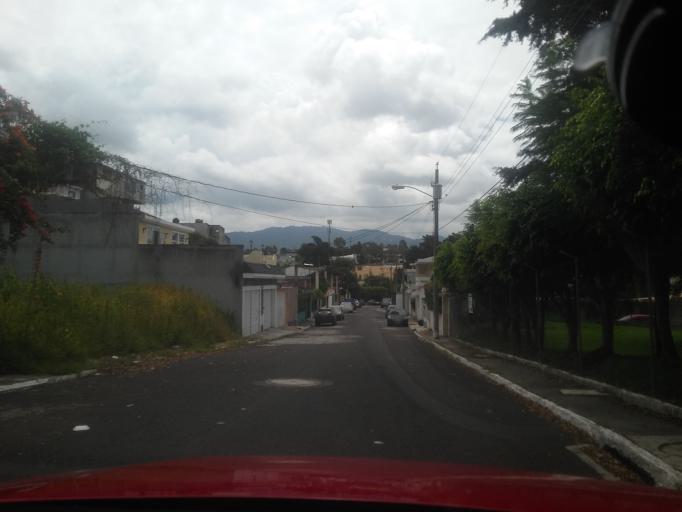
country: GT
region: Guatemala
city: Mixco
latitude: 14.6467
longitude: -90.5659
